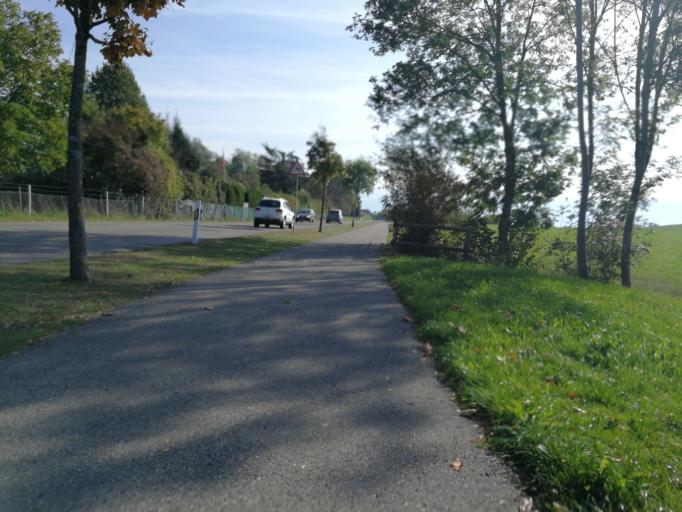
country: CH
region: Zurich
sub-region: Bezirk Hinwil
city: Hinwil
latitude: 47.2950
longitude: 8.8515
